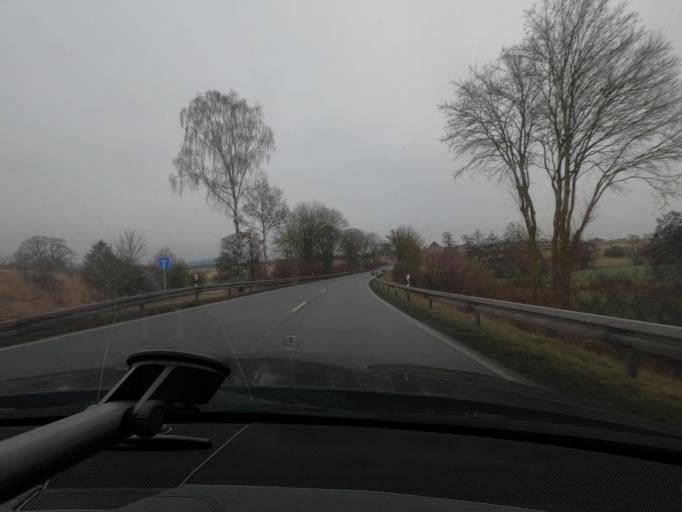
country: DE
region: Hesse
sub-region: Regierungsbezirk Kassel
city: Wolfhagen
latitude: 51.3325
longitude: 9.1486
